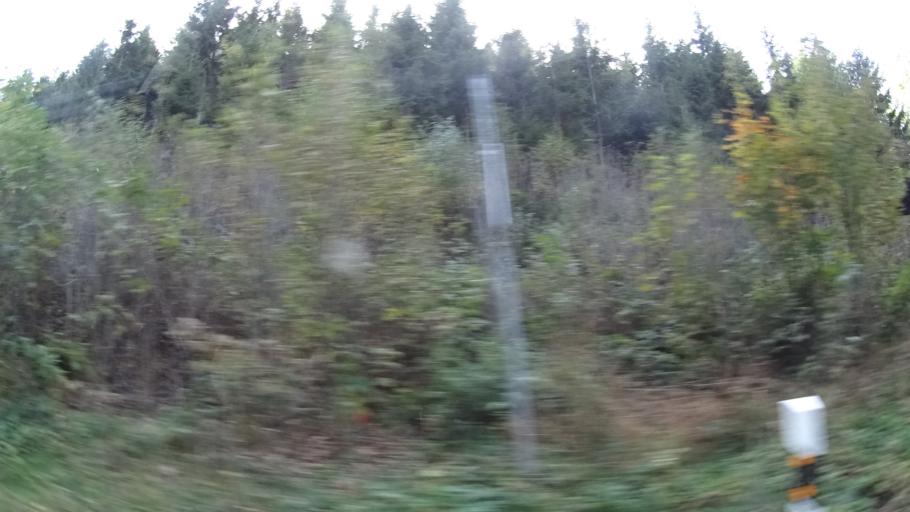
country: DE
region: Thuringia
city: Bermbach
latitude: 50.7007
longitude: 10.6284
